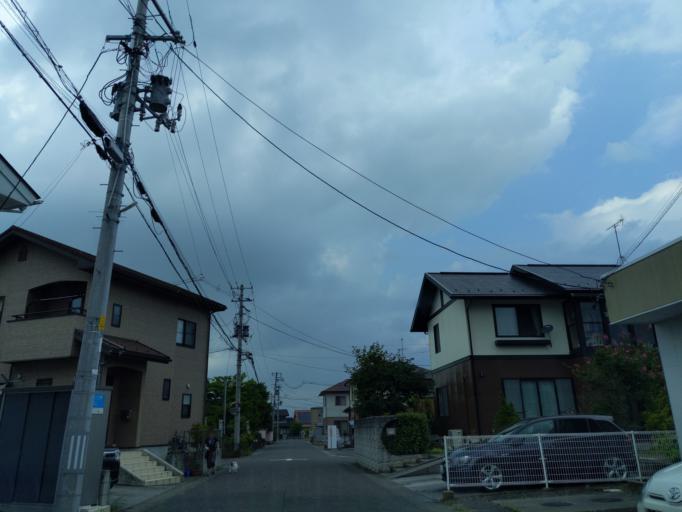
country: JP
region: Fukushima
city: Koriyama
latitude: 37.4275
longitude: 140.3724
